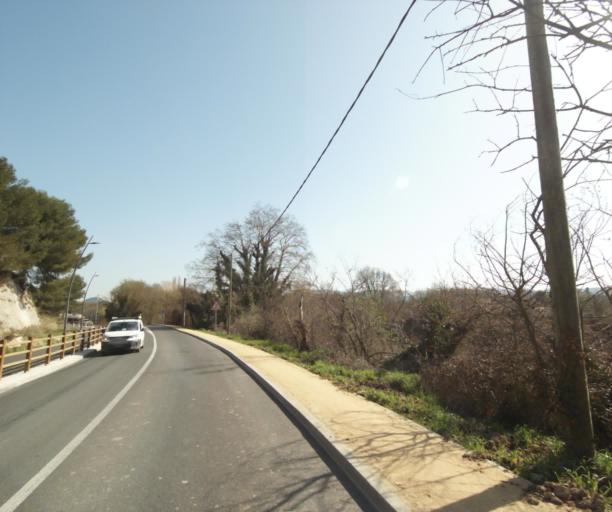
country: FR
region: Provence-Alpes-Cote d'Azur
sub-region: Departement des Bouches-du-Rhone
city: Bouc-Bel-Air
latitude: 43.4454
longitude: 5.4047
